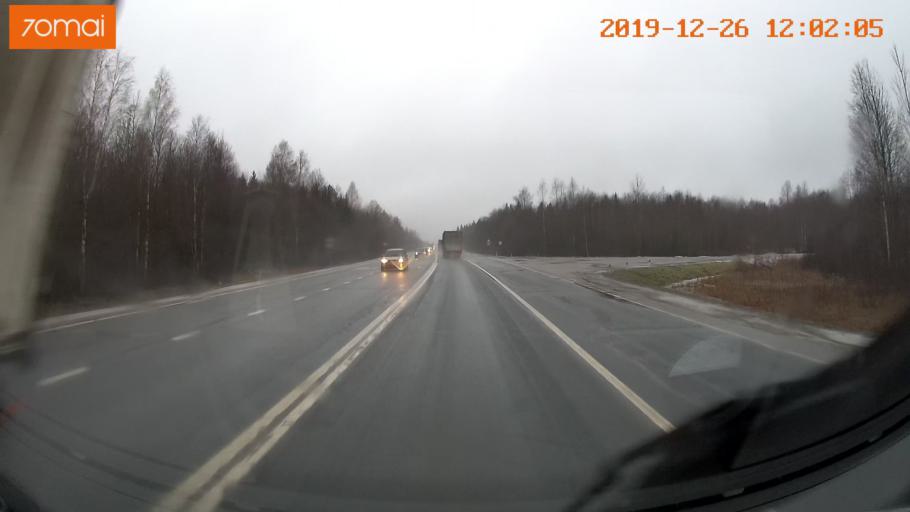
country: RU
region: Vologda
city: Tonshalovo
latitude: 59.3068
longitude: 38.1566
